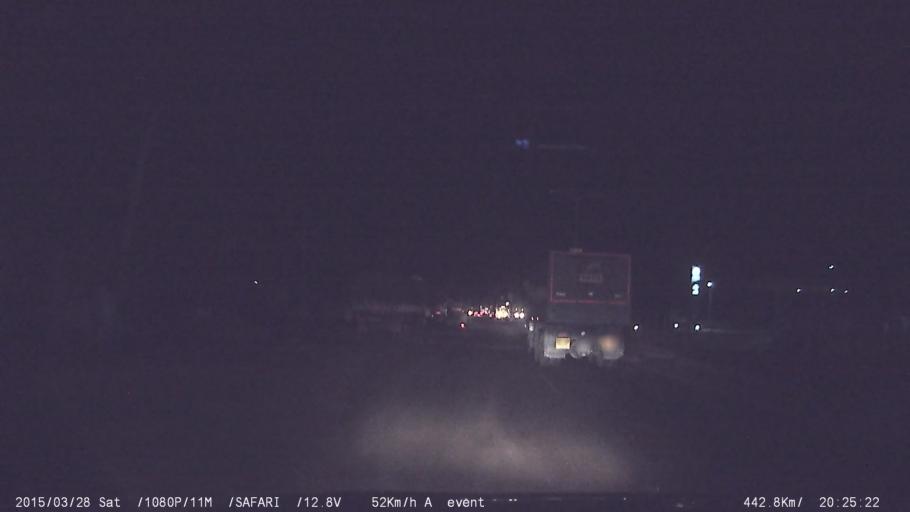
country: IN
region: Karnataka
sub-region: Mandya
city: Maddur
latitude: 12.5980
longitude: 77.0526
